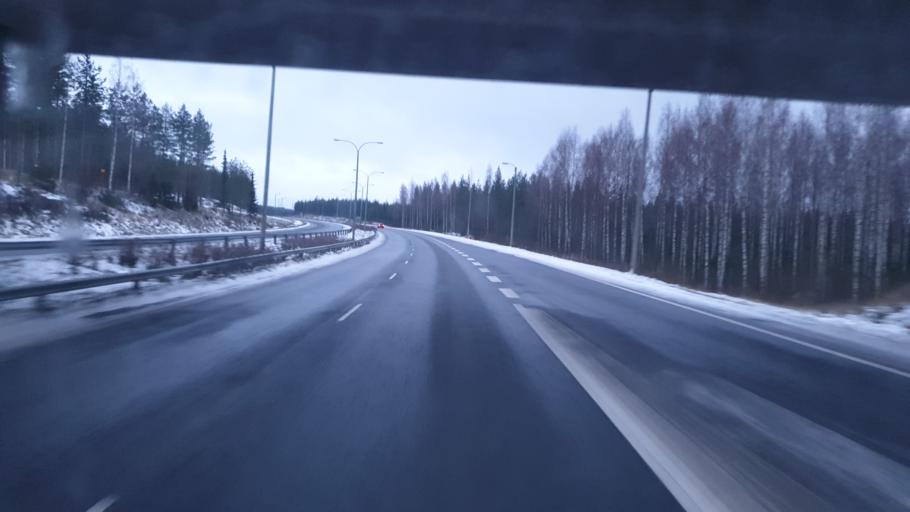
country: FI
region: Northern Savo
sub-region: Kuopio
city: Siilinjaervi
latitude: 63.0179
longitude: 27.6634
